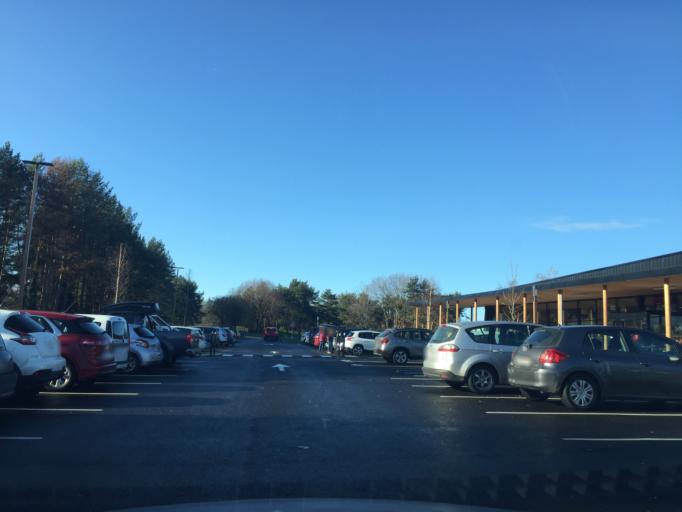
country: FR
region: Auvergne
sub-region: Departement du Puy-de-Dome
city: Orleat
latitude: 45.8504
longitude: 3.4068
